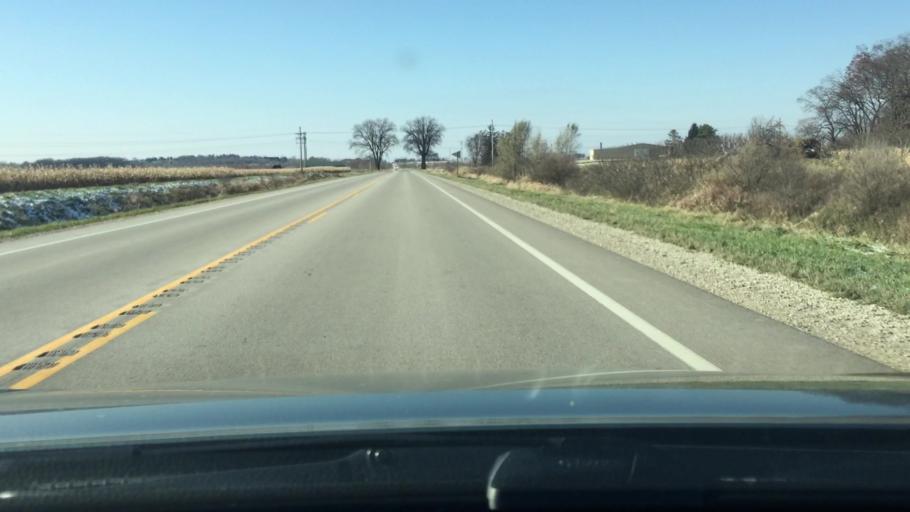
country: US
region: Wisconsin
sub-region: Jefferson County
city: Jefferson
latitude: 43.0071
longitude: -88.8593
